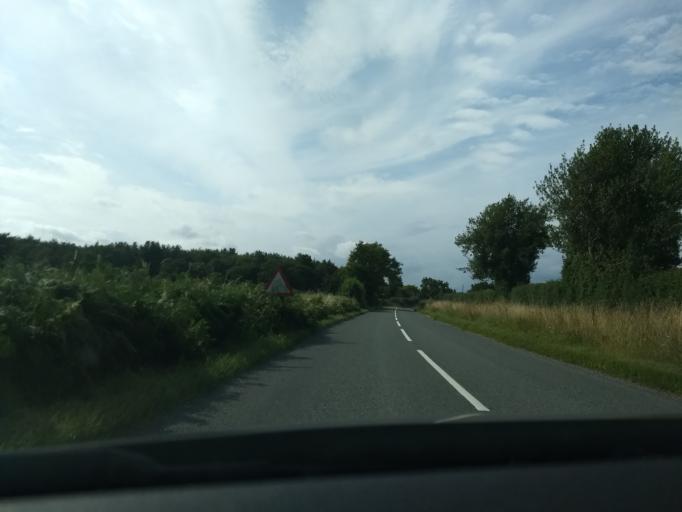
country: GB
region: England
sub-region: Suffolk
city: Ipswich
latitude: 51.9959
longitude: 1.1894
